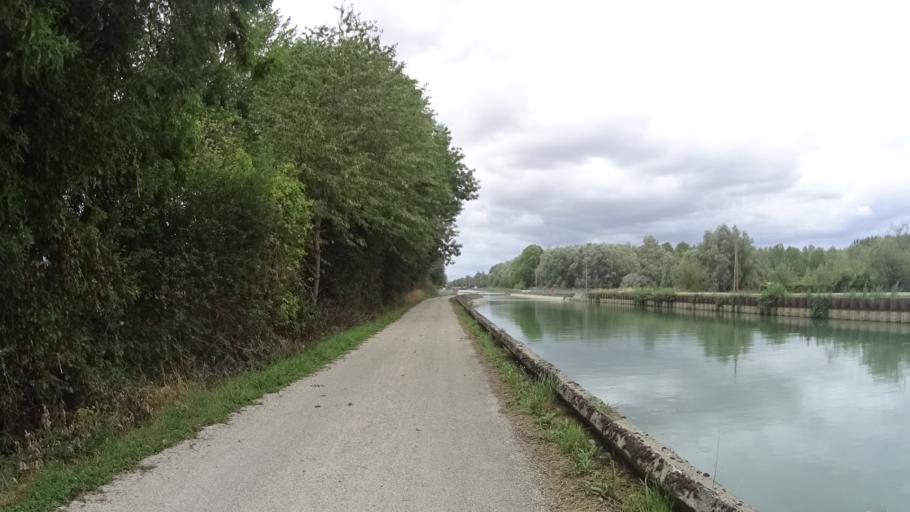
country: FR
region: Picardie
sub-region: Departement de l'Aisne
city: La Fere
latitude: 49.6851
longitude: 3.3647
